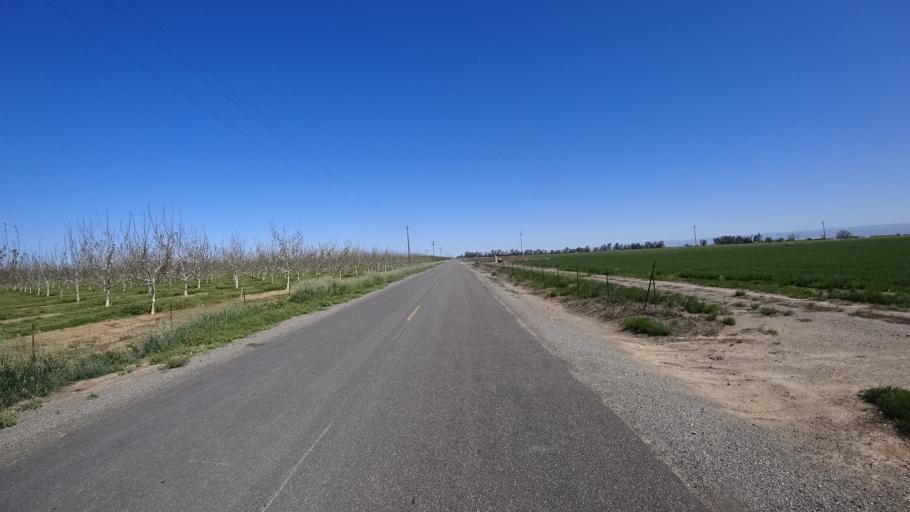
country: US
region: California
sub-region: Glenn County
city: Hamilton City
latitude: 39.6754
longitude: -122.1033
